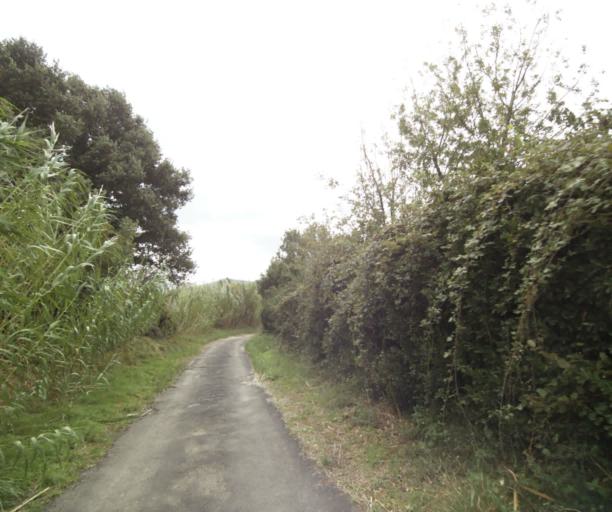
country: FR
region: Languedoc-Roussillon
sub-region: Departement des Pyrenees-Orientales
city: Argelers
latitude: 42.5530
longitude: 3.0338
